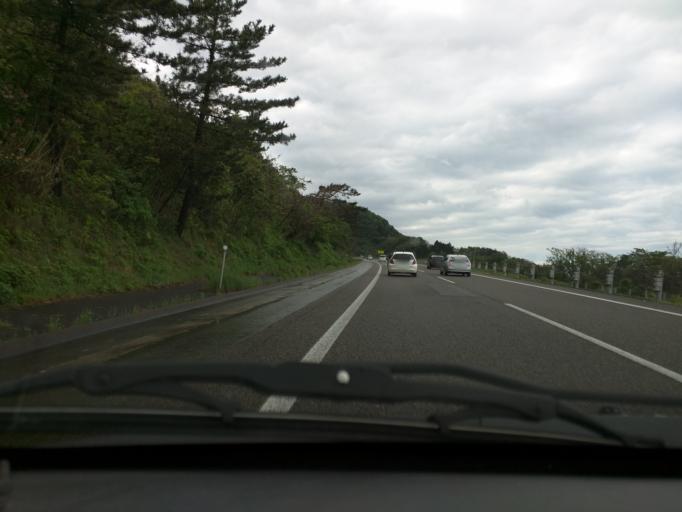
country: JP
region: Niigata
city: Kashiwazaki
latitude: 37.3070
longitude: 138.4214
